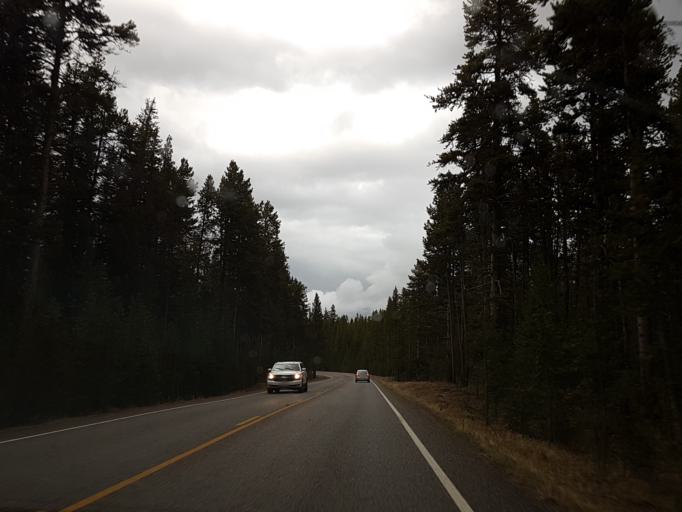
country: US
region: Montana
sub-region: Gallatin County
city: West Yellowstone
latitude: 44.4579
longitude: -110.5087
